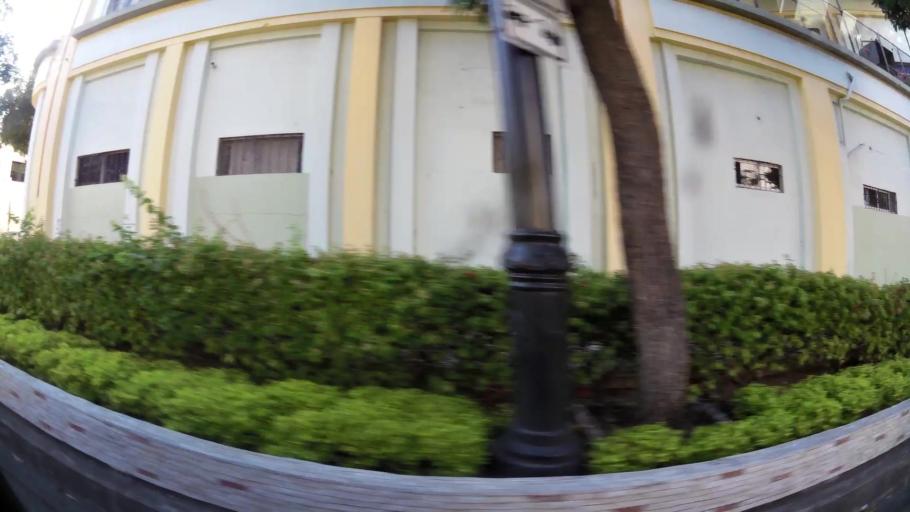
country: EC
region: Guayas
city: Eloy Alfaro
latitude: -2.1833
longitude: -79.8776
